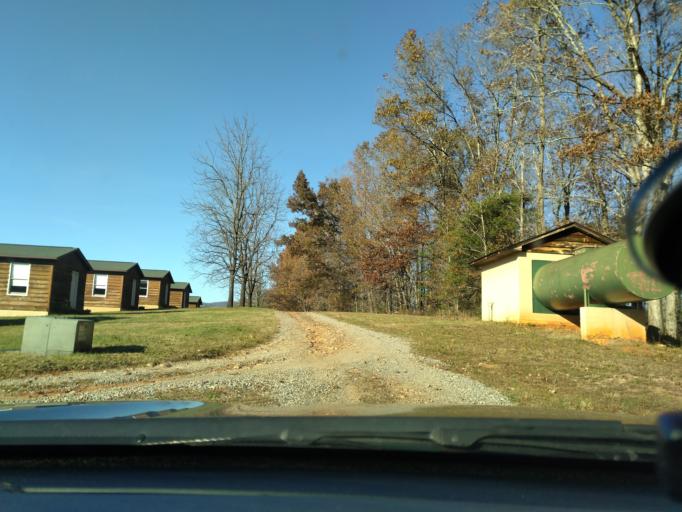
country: US
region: Virginia
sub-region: Floyd County
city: Floyd
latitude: 36.8358
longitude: -80.1815
